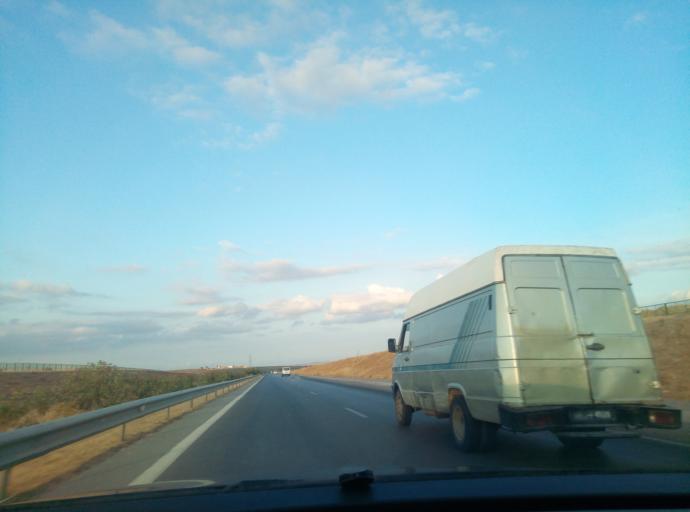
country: TN
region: Manouba
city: El Battan
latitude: 36.6620
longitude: 9.8483
